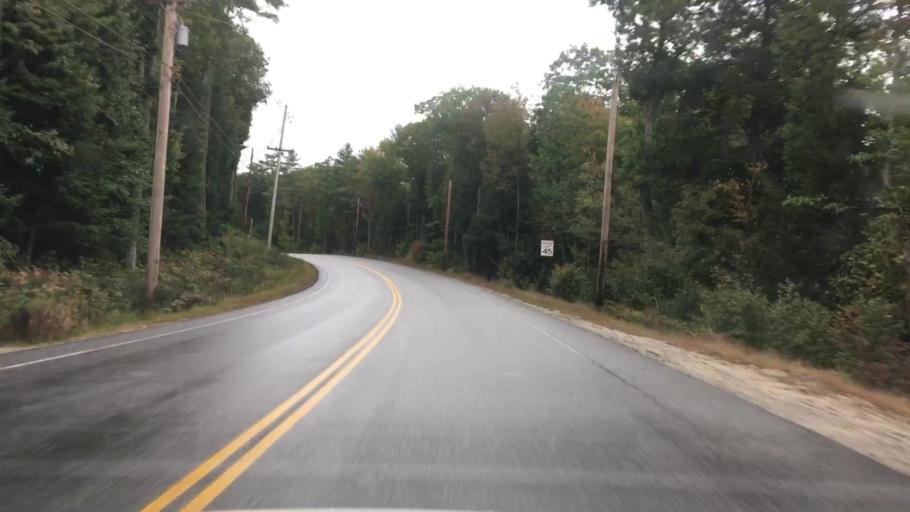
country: US
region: Maine
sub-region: Cumberland County
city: Raymond
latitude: 43.9862
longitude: -70.5495
